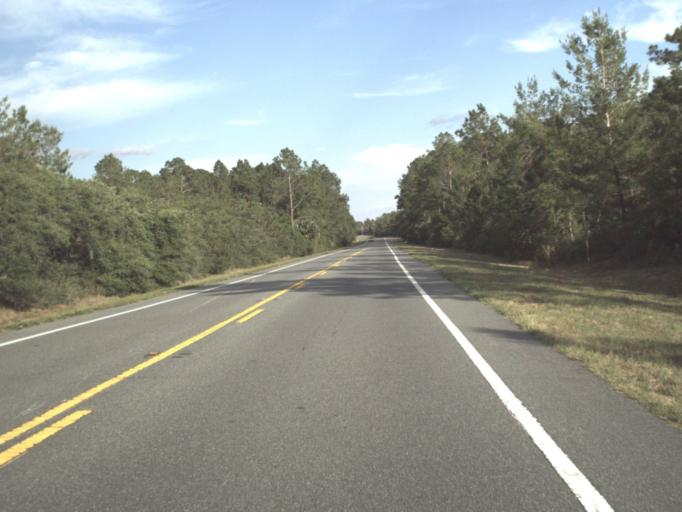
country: US
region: Florida
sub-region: Lake County
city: Astor
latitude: 29.1656
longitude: -81.6093
